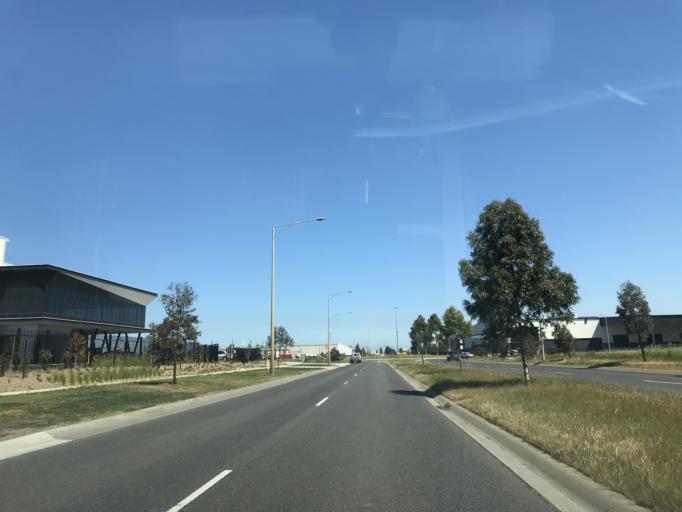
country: AU
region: Victoria
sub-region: Wyndham
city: Truganina
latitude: -37.8216
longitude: 144.7647
